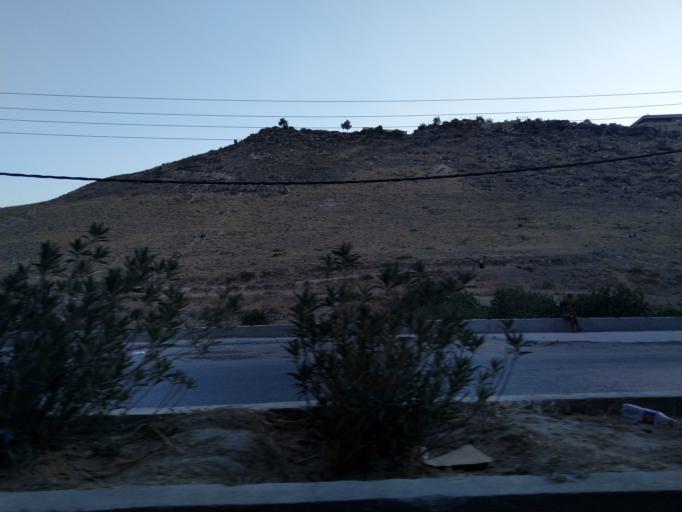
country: SY
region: Rif-dimashq
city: At Tall
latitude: 33.5745
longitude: 36.3039
